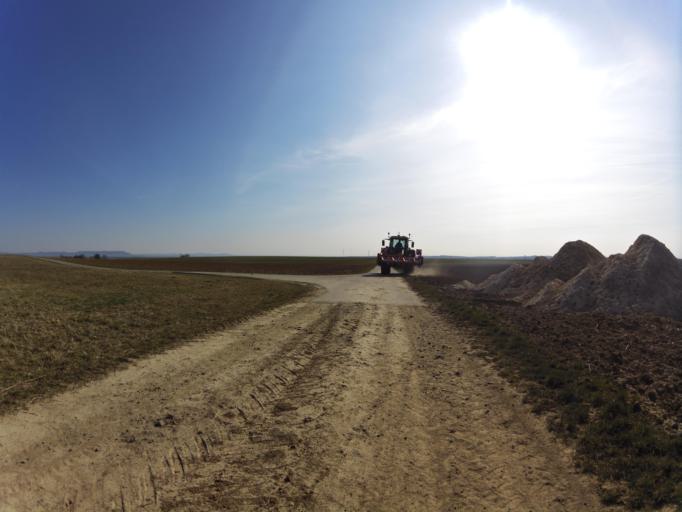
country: DE
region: Bavaria
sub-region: Regierungsbezirk Unterfranken
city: Prosselsheim
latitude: 49.8374
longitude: 10.1214
